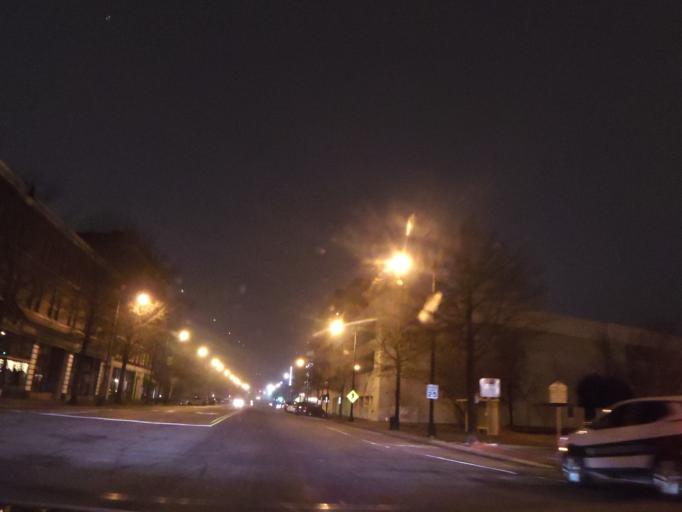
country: US
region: North Carolina
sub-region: Cumberland County
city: Fayetteville
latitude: 35.0540
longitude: -78.8822
